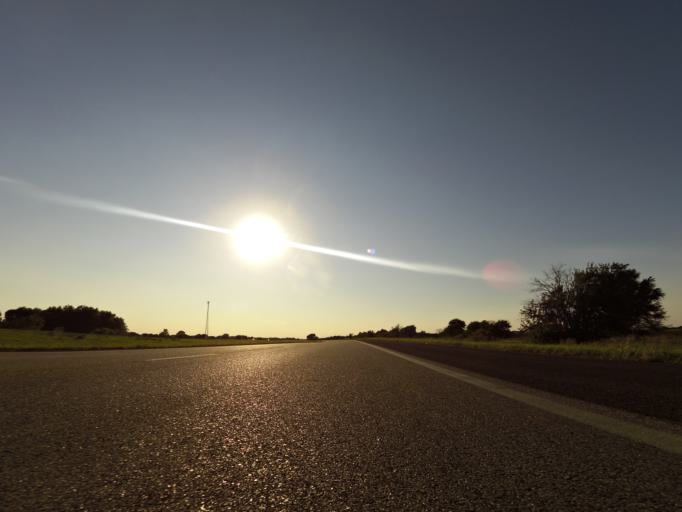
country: US
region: Kansas
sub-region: Reno County
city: Haven
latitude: 37.8936
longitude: -97.7631
